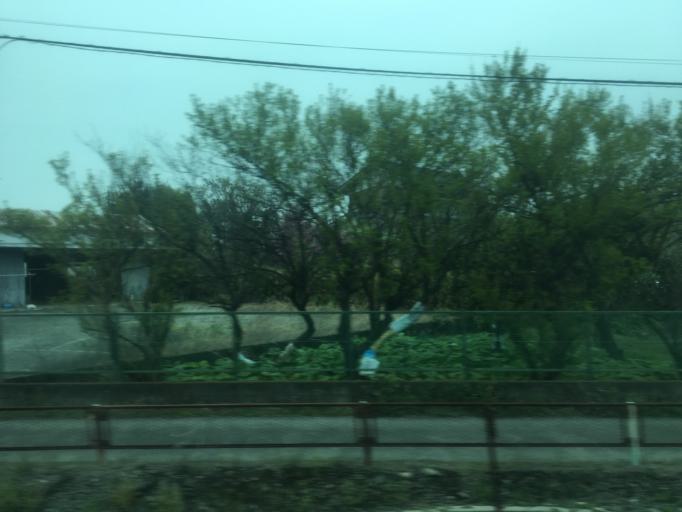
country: JP
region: Saitama
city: Fukiage-fujimi
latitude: 36.1195
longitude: 139.4252
